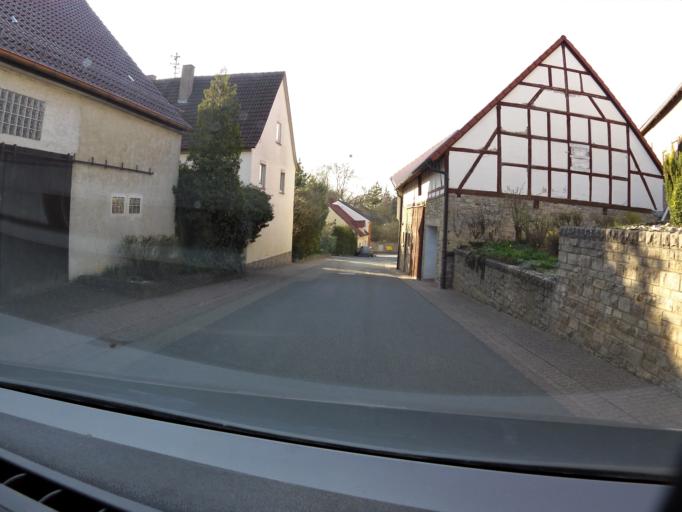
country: DE
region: Baden-Wuerttemberg
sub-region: Regierungsbezirk Stuttgart
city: Grunsfeld
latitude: 49.5749
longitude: 9.7900
